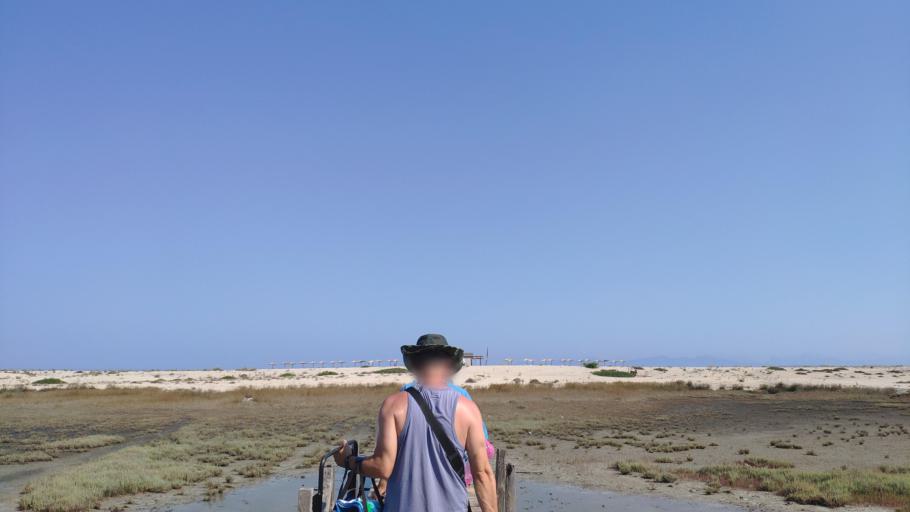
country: GR
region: Ionian Islands
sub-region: Lefkada
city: Lefkada
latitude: 38.8517
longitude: 20.7364
